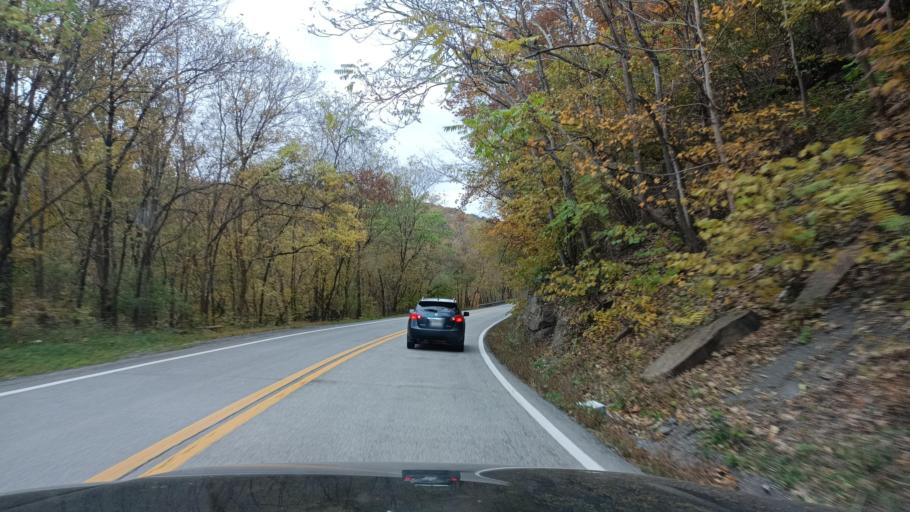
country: US
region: West Virginia
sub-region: Taylor County
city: Grafton
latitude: 39.3419
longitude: -79.9703
